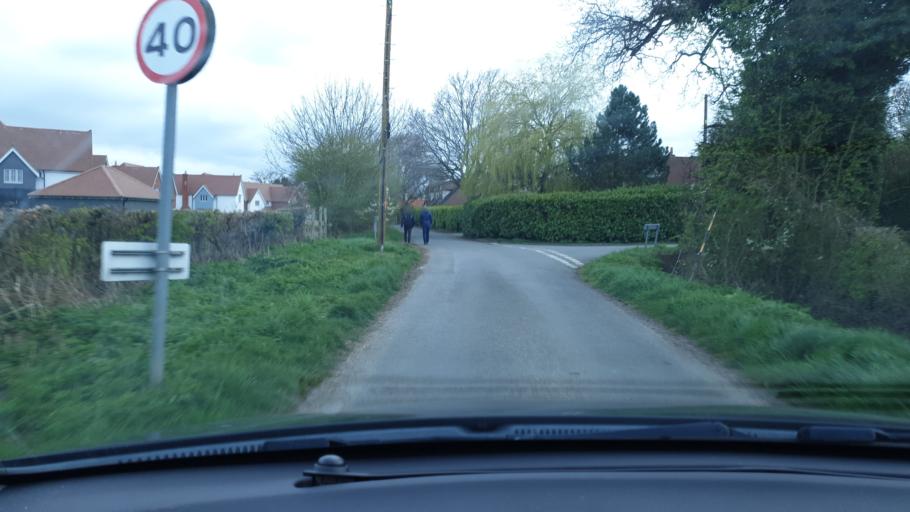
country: GB
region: England
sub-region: Essex
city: Mistley
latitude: 51.8917
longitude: 1.1113
